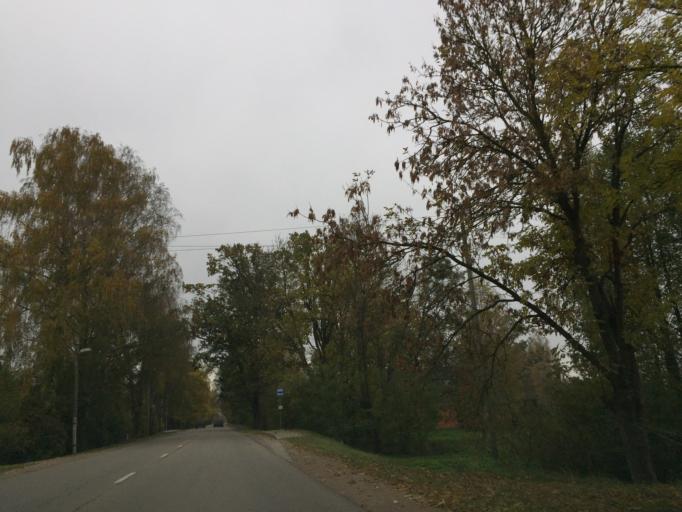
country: LV
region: Jelgava
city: Jelgava
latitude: 56.6749
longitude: 23.7266
